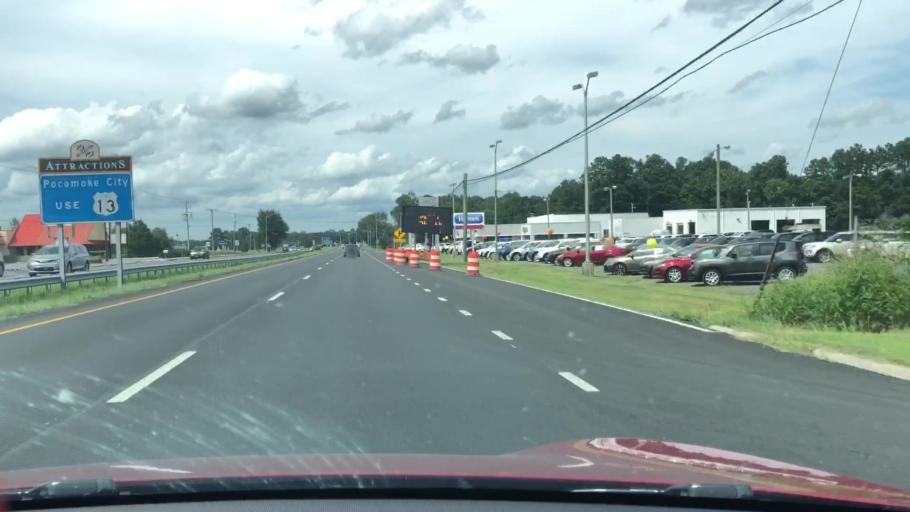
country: US
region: Maryland
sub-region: Worcester County
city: Pocomoke City
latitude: 38.0523
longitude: -75.5434
